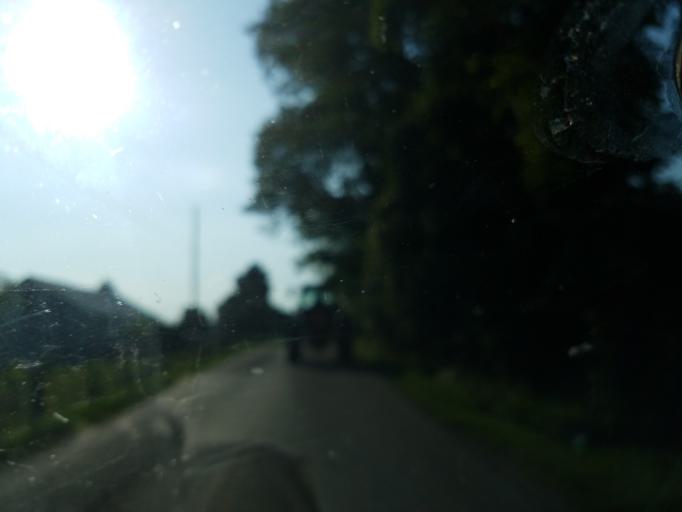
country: US
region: Ohio
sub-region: Adams County
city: West Union
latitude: 38.8878
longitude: -83.5096
